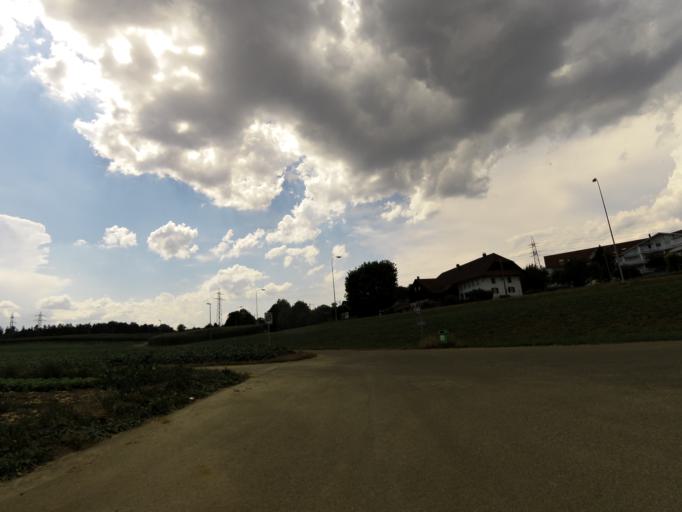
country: CH
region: Aargau
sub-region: Bezirk Lenzburg
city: Othmarsingen
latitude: 47.3966
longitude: 8.2074
